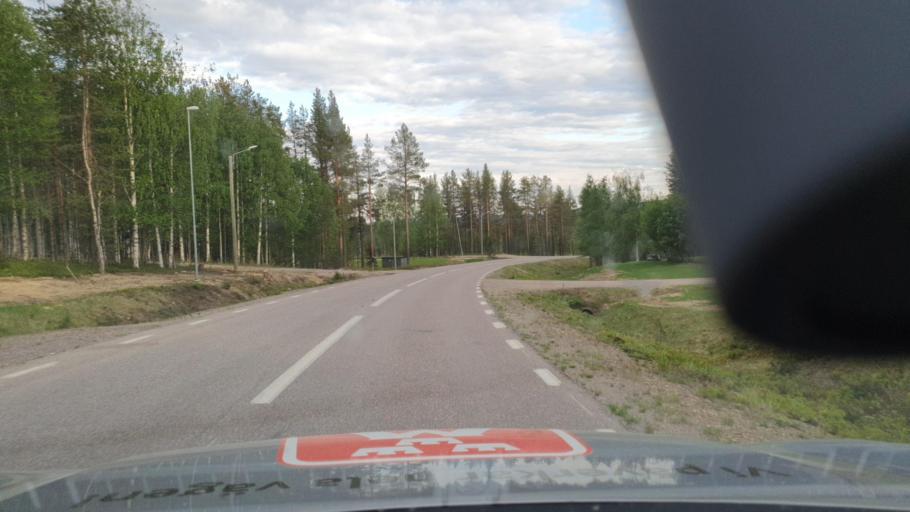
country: SE
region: Norrbotten
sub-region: Gallivare Kommun
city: Gaellivare
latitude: 66.9326
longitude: 21.2705
